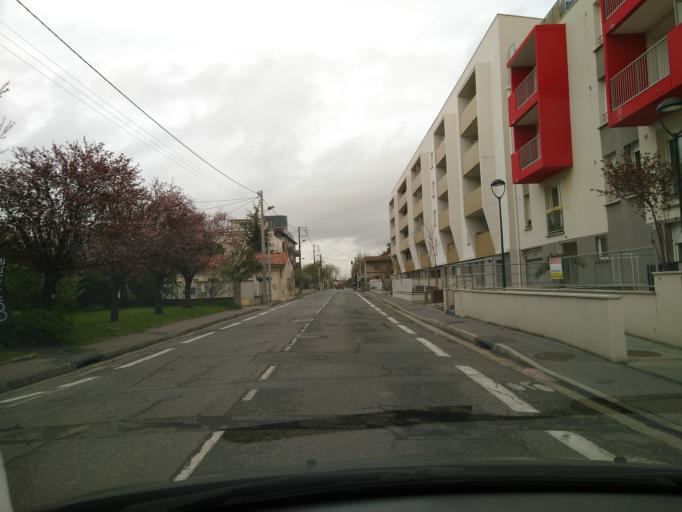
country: FR
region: Midi-Pyrenees
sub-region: Departement de la Haute-Garonne
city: Toulouse
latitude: 43.6300
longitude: 1.4379
